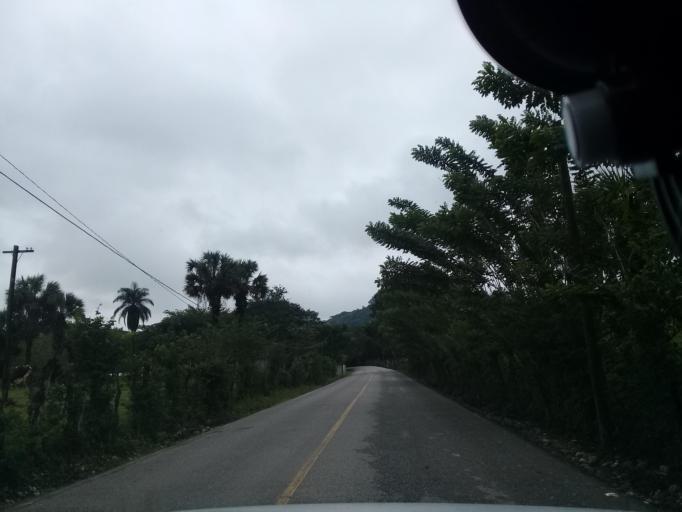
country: MX
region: Veracruz
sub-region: Chalma
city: San Pedro Coyutla
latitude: 21.2191
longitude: -98.4299
